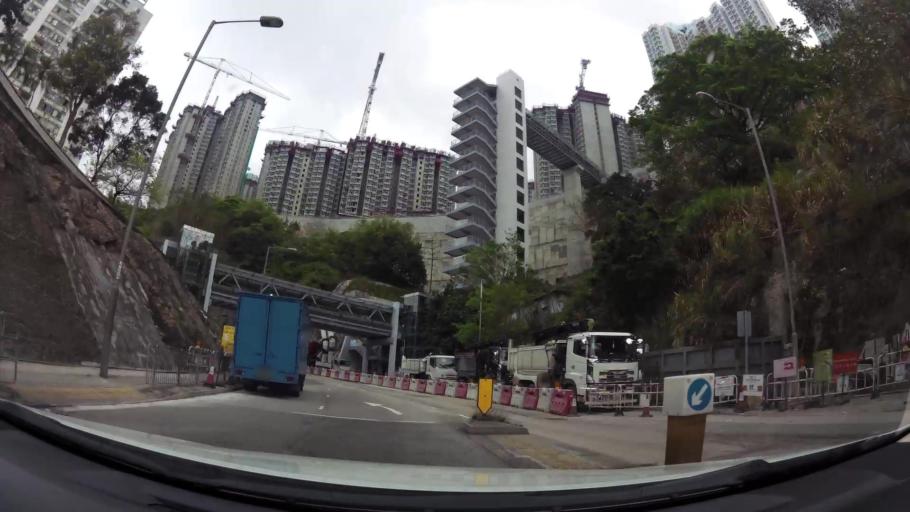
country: HK
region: Kowloon City
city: Kowloon
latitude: 22.3251
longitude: 114.2290
